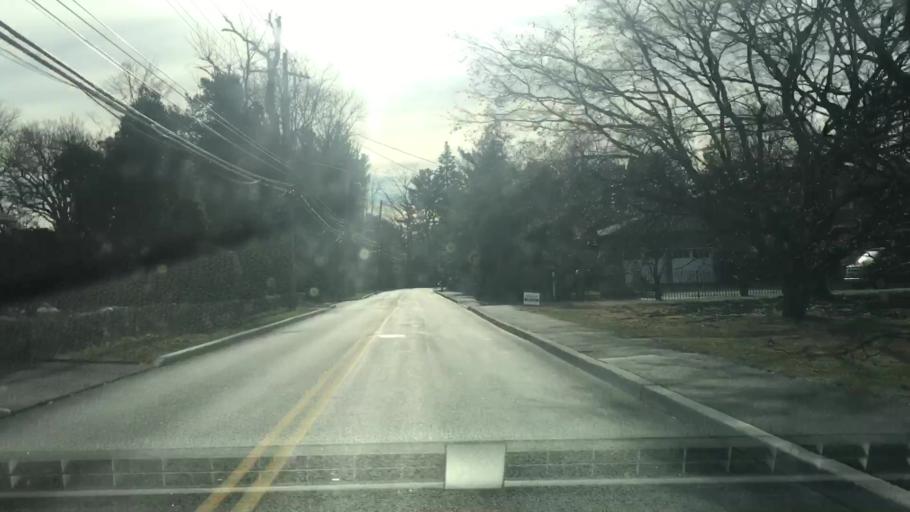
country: US
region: New York
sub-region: Westchester County
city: Greenville
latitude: 40.9905
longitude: -73.8282
